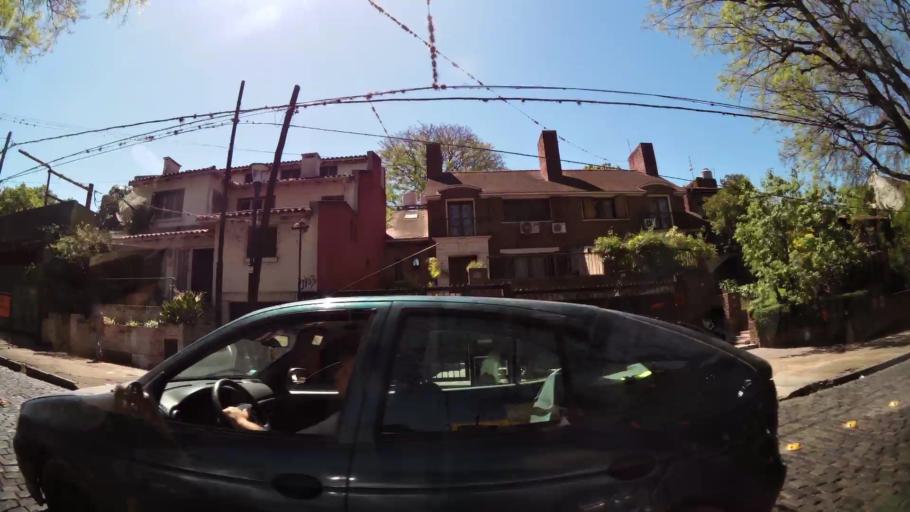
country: AR
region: Buenos Aires
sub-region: Partido de San Isidro
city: San Isidro
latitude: -34.4661
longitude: -58.5127
